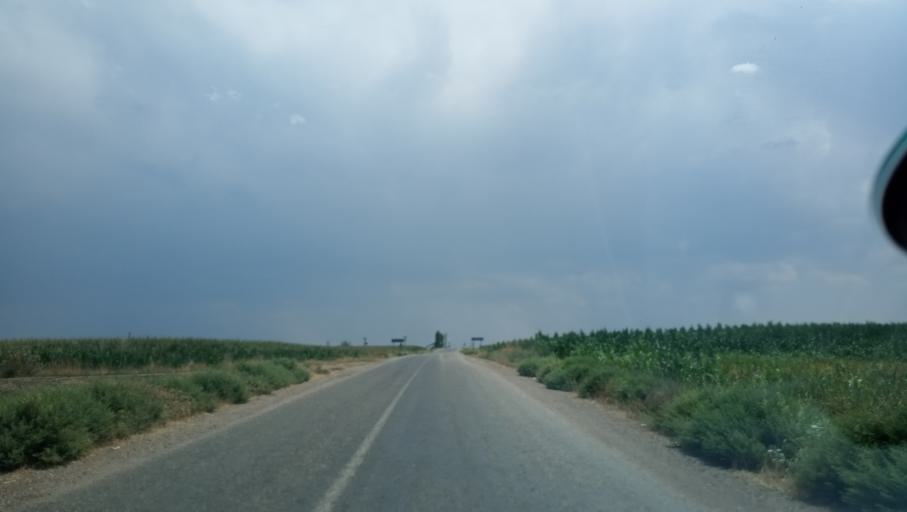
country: TR
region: Diyarbakir
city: Tepe
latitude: 37.7268
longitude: 40.8270
